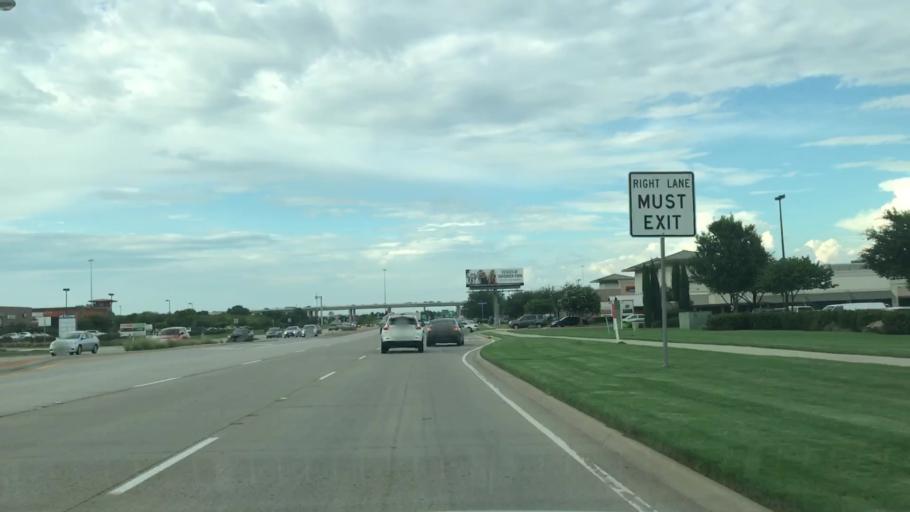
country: US
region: Texas
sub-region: Collin County
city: Frisco
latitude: 33.0902
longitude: -96.8054
